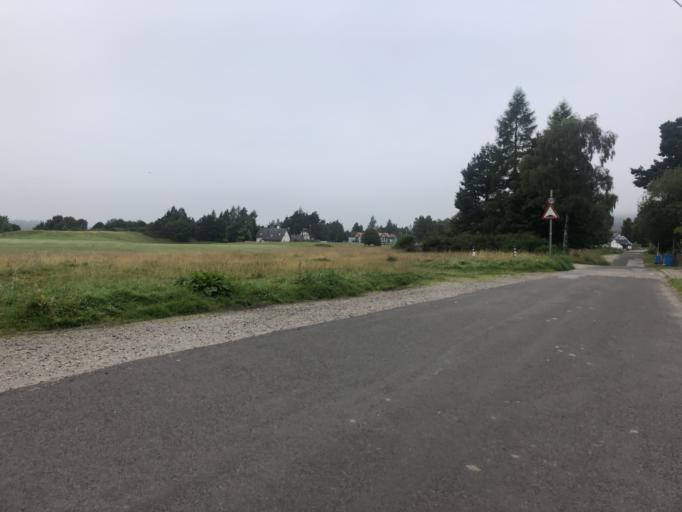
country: GB
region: Scotland
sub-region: Highland
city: Kingussie
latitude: 57.0657
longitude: -4.1144
